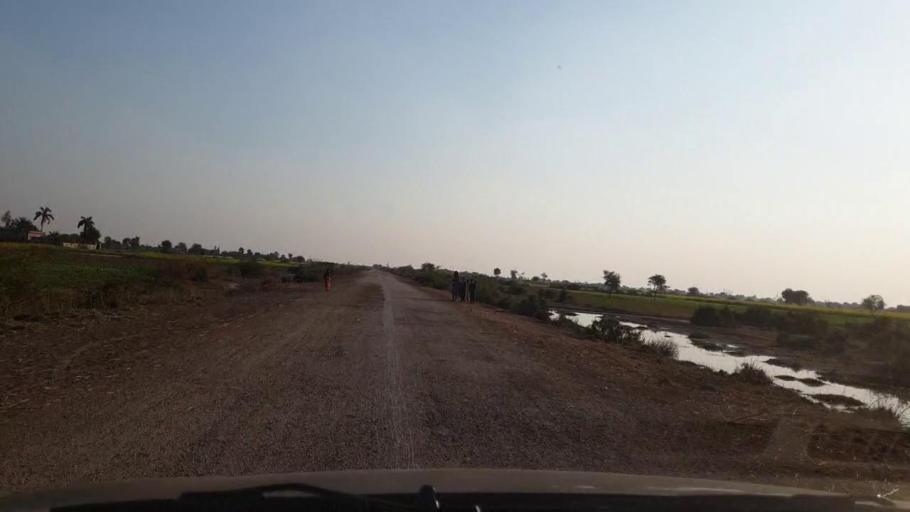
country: PK
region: Sindh
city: Jhol
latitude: 25.9279
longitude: 68.9081
